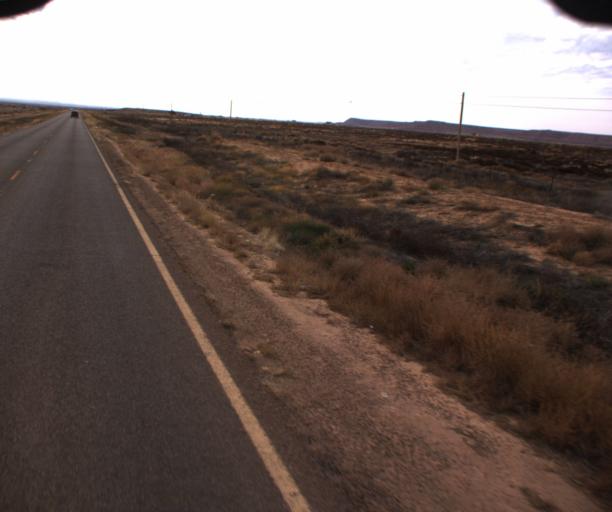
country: US
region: Arizona
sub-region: Apache County
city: Many Farms
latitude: 36.3230
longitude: -109.6177
